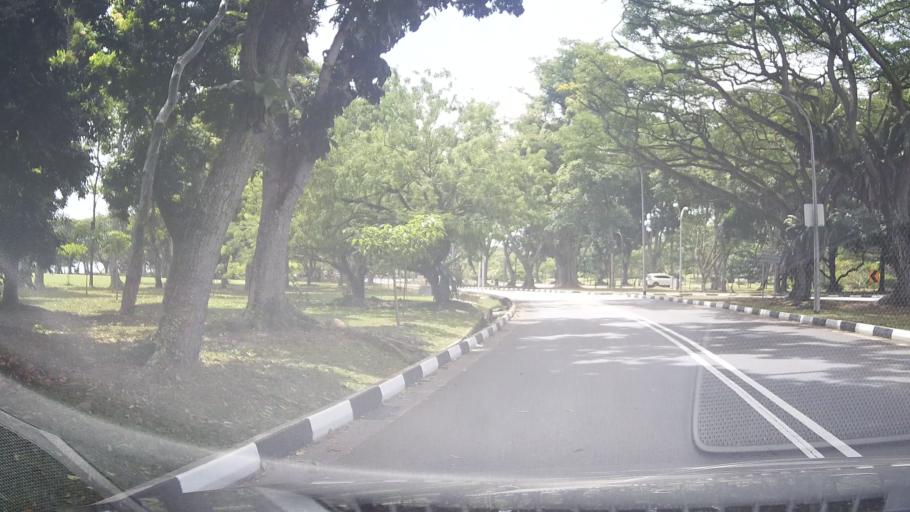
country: SG
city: Singapore
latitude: 1.3094
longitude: 103.9373
